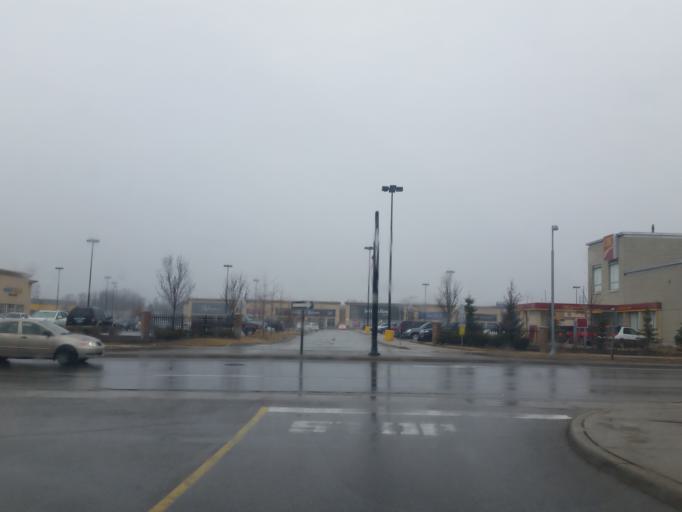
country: CA
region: Ontario
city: Oshawa
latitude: 43.8798
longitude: -78.8786
